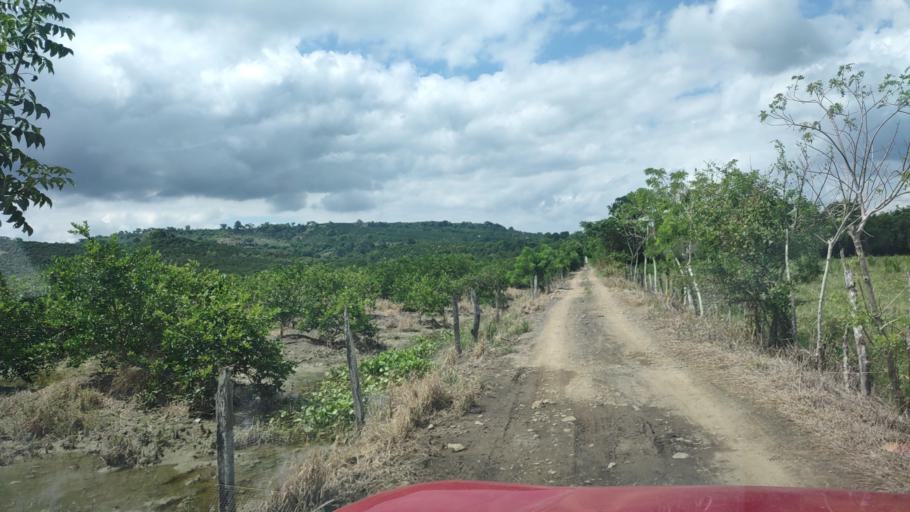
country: MX
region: Puebla
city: San Jose Acateno
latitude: 20.2210
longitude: -97.1464
